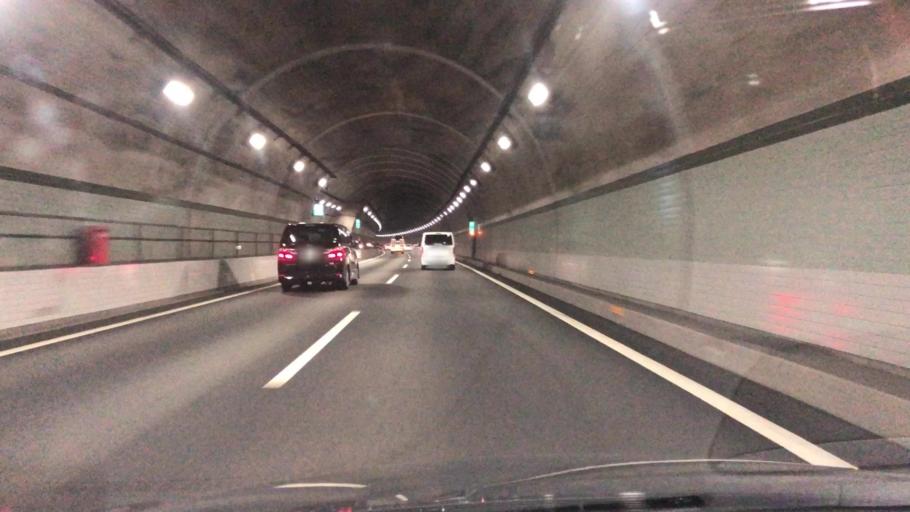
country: JP
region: Tokyo
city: Itsukaichi
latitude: 35.6909
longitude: 139.2628
